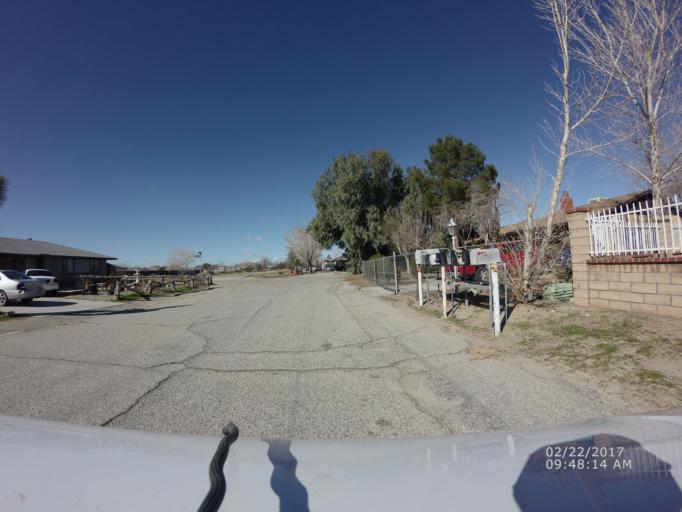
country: US
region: California
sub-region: Los Angeles County
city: Lake Los Angeles
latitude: 34.6224
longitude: -117.8425
